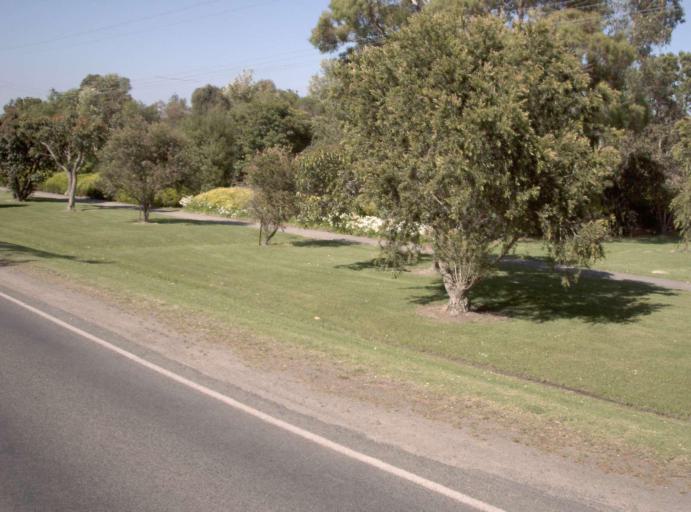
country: AU
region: Victoria
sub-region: Latrobe
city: Traralgon
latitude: -38.5700
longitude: 146.6745
